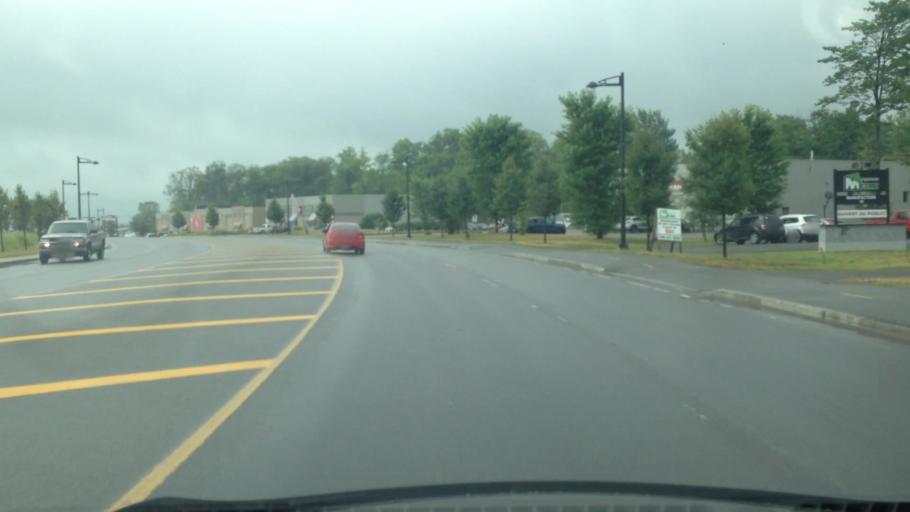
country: CA
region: Quebec
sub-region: Laurentides
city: Saint-Jerome
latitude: 45.7594
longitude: -74.0251
